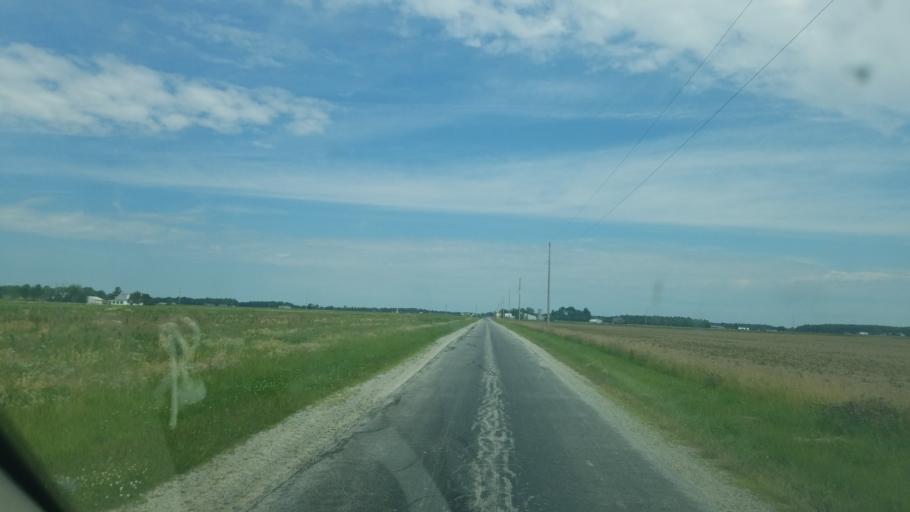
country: US
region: Ohio
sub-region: Wood County
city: North Baltimore
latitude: 41.2286
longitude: -83.5732
